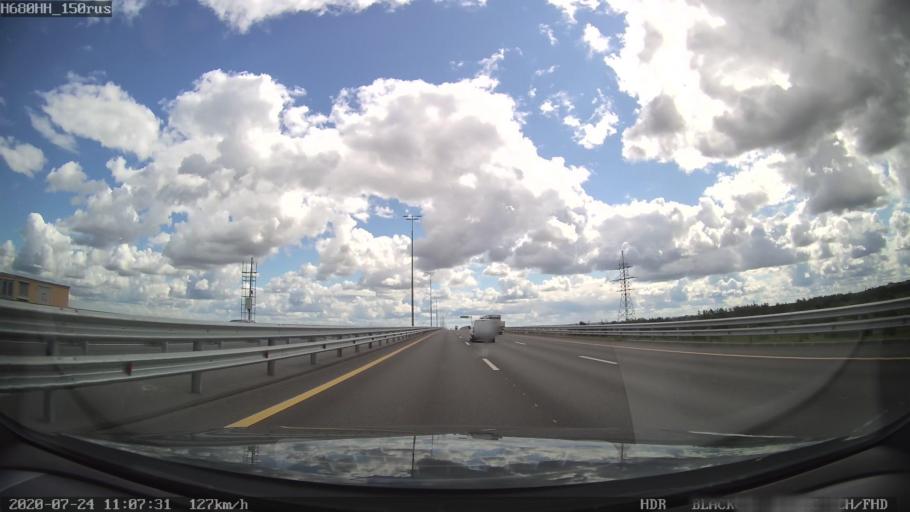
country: RU
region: St.-Petersburg
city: Pushkin
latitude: 59.7556
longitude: 30.4077
